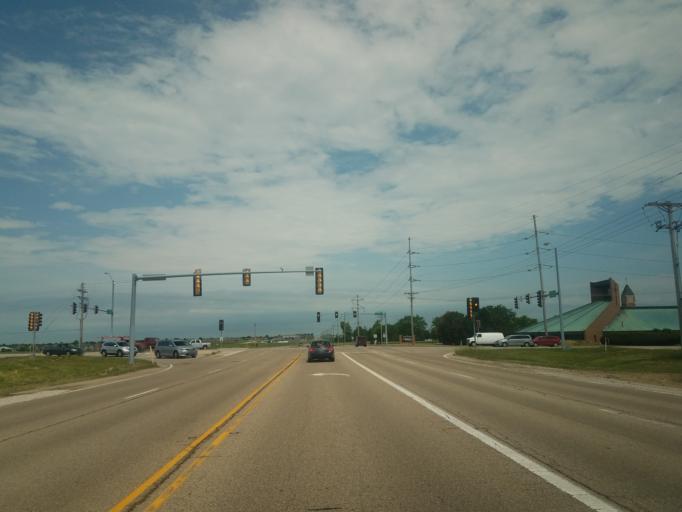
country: US
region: Illinois
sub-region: McLean County
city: Bloomington
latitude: 40.4874
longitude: -88.9025
